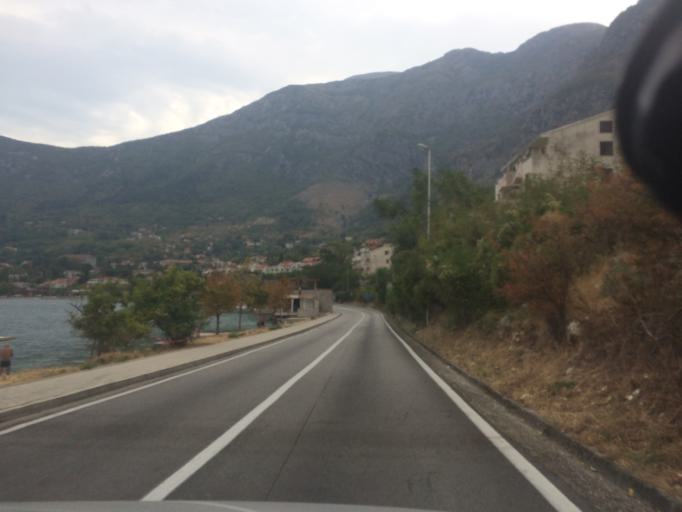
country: ME
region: Kotor
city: Risan
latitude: 42.5062
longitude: 18.6940
